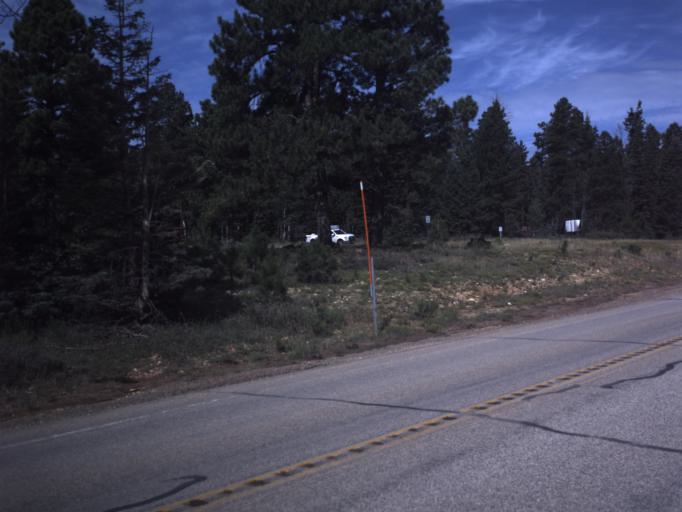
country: US
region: Utah
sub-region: Garfield County
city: Panguitch
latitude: 37.5173
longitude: -112.6455
